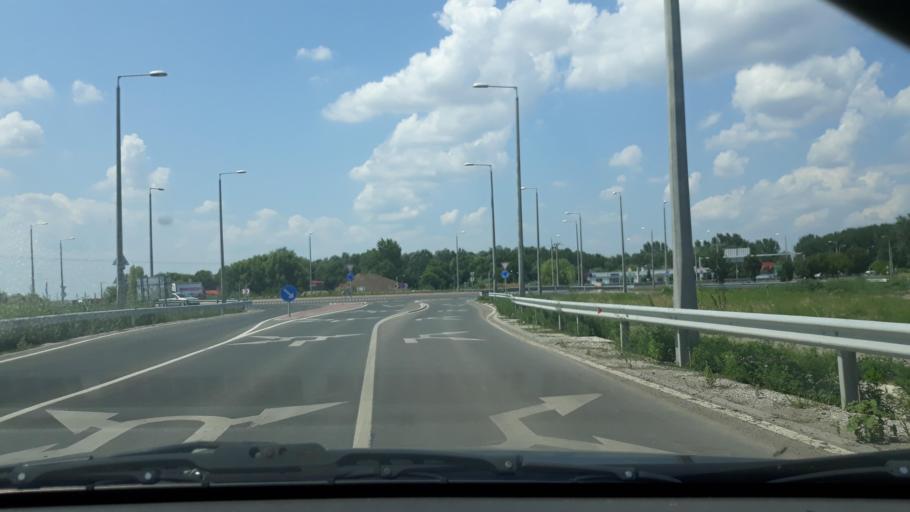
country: HU
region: Hajdu-Bihar
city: Mikepercs
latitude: 47.4850
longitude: 21.6344
